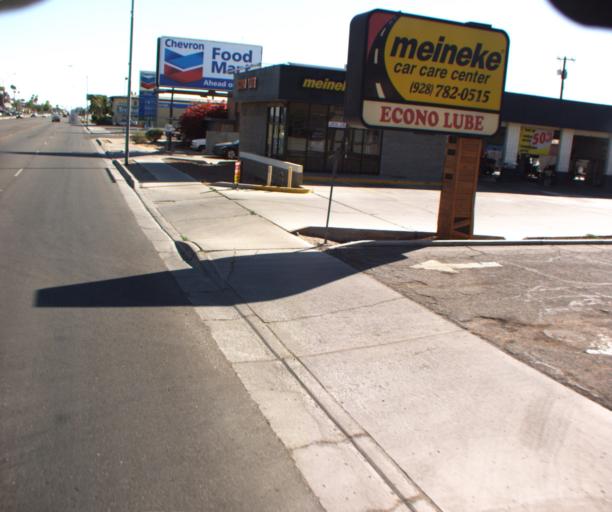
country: US
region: Arizona
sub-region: Yuma County
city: Yuma
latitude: 32.6923
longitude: -114.6247
